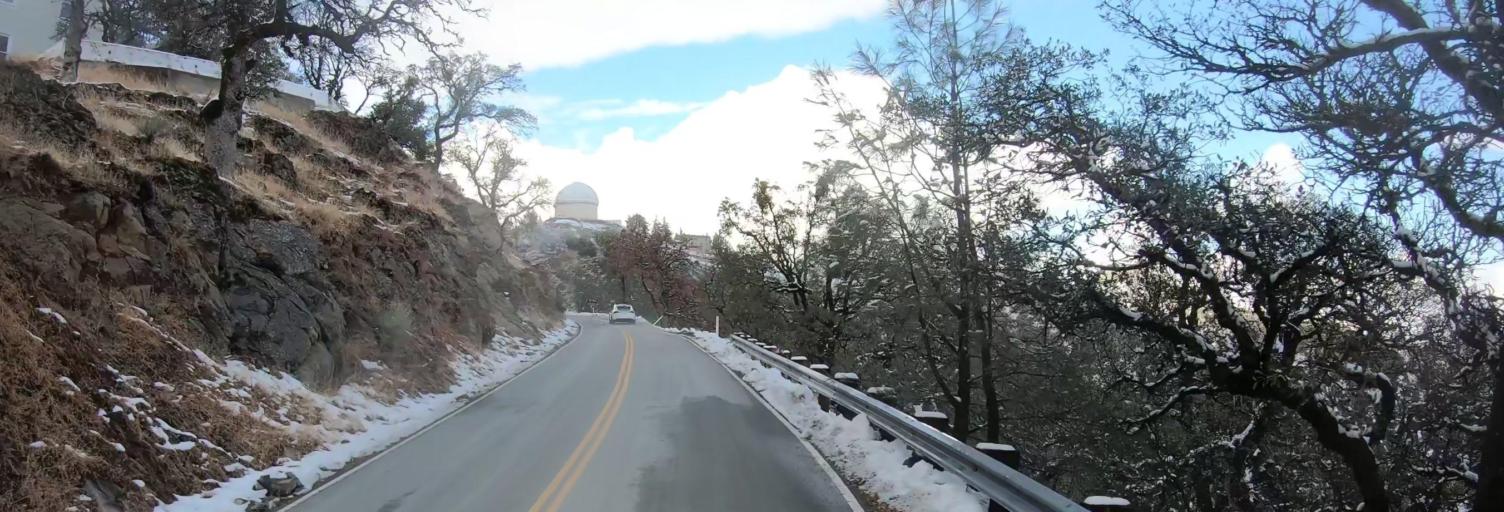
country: US
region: California
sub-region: Santa Clara County
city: East Foothills
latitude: 37.3374
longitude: -121.6438
